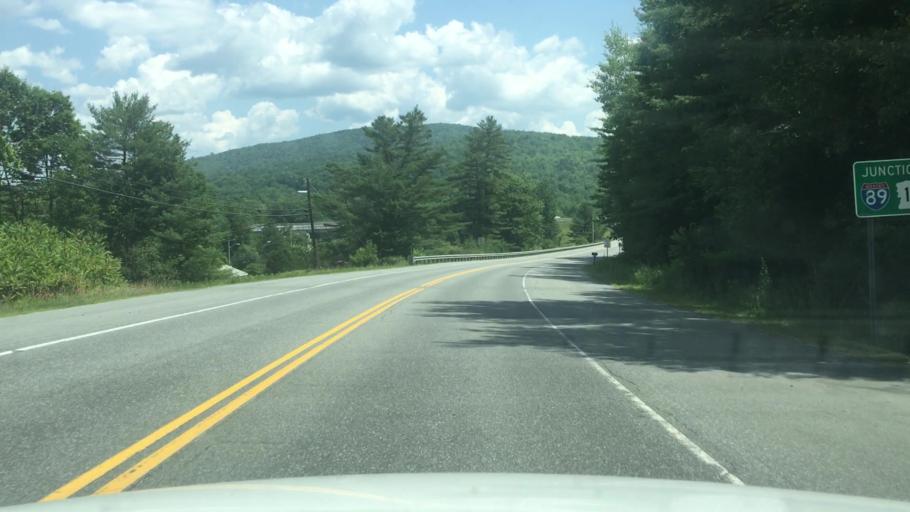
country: US
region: New Hampshire
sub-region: Grafton County
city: Lebanon
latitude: 43.6370
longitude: -72.2171
